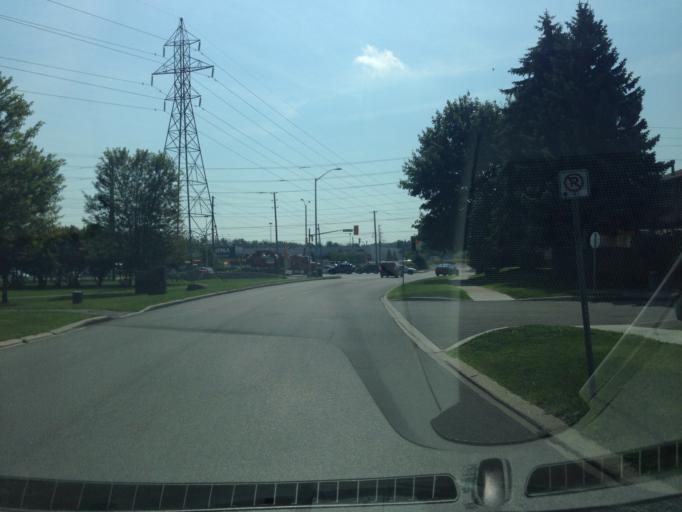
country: CA
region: Ontario
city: Ottawa
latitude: 45.4182
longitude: -75.6014
